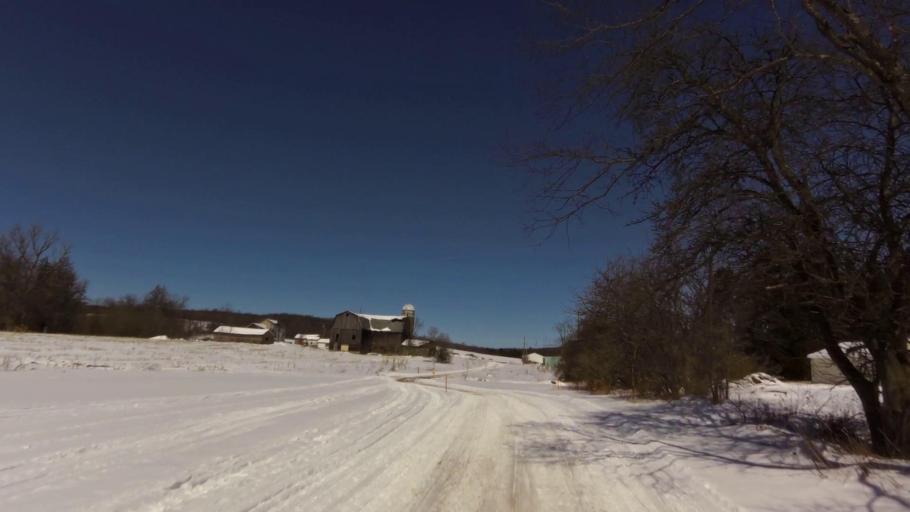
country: US
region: New York
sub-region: Allegany County
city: Houghton
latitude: 42.3904
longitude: -78.2586
